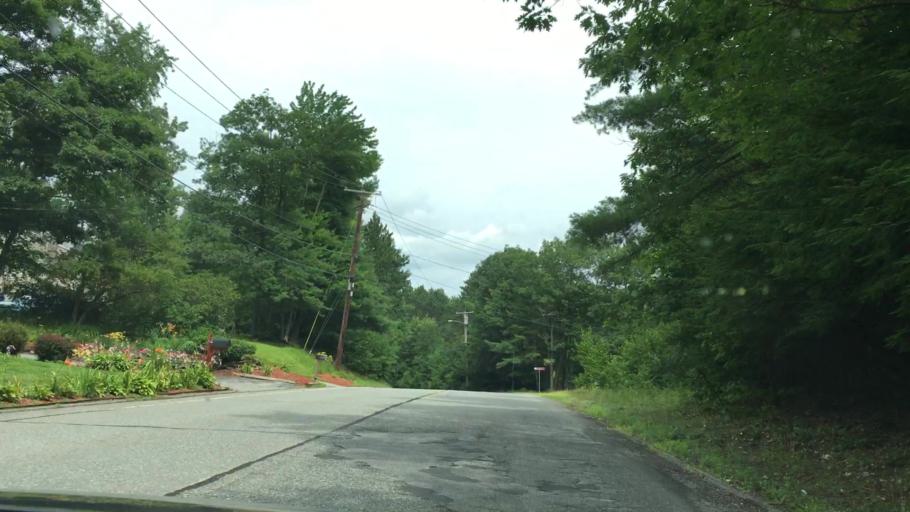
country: US
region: Massachusetts
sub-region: Worcester County
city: Winchendon
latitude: 42.6853
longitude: -72.0180
